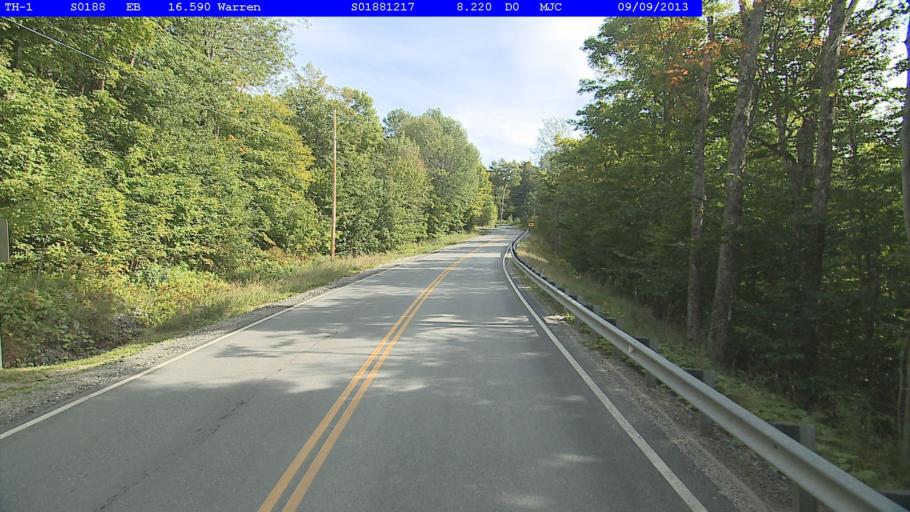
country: US
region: Vermont
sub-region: Washington County
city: Northfield
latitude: 44.1045
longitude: -72.7939
